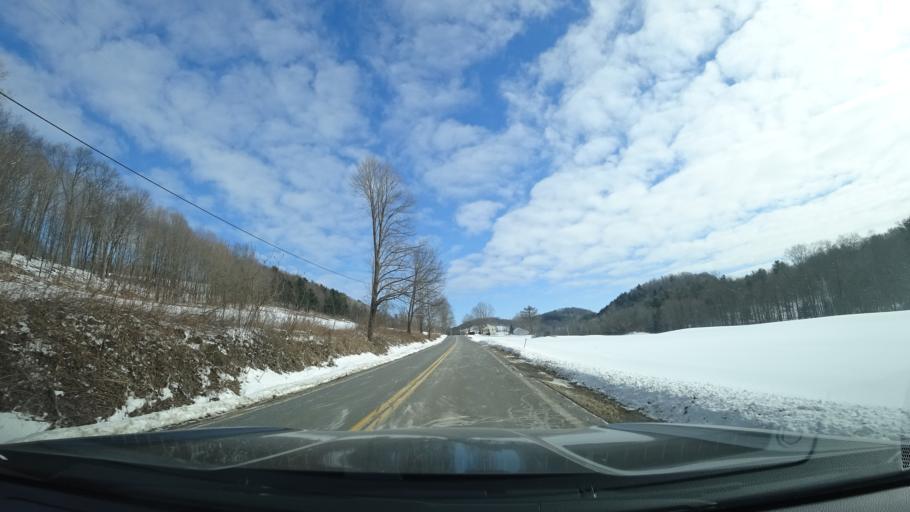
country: US
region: New York
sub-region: Washington County
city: Fort Edward
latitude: 43.2490
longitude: -73.4283
